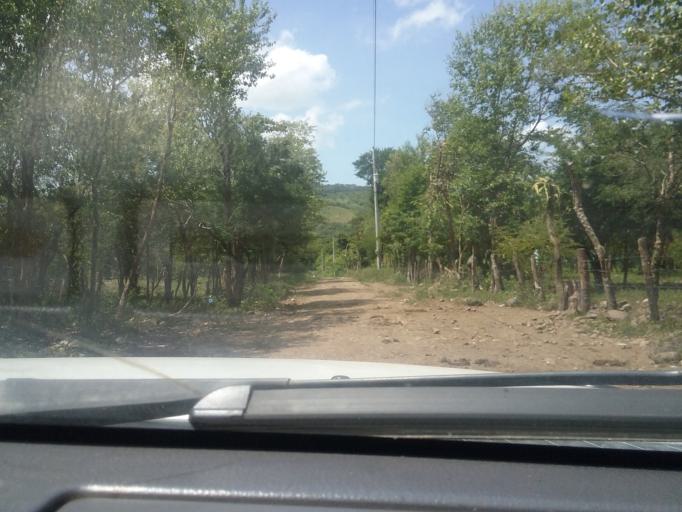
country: NI
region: Matagalpa
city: Terrabona
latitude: 12.6520
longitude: -85.9945
